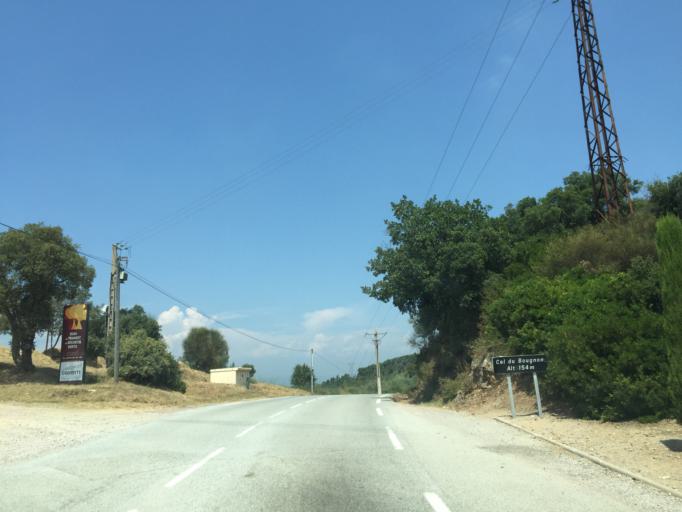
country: FR
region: Provence-Alpes-Cote d'Azur
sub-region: Departement du Var
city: Sainte-Maxime
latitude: 43.3633
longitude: 6.6734
